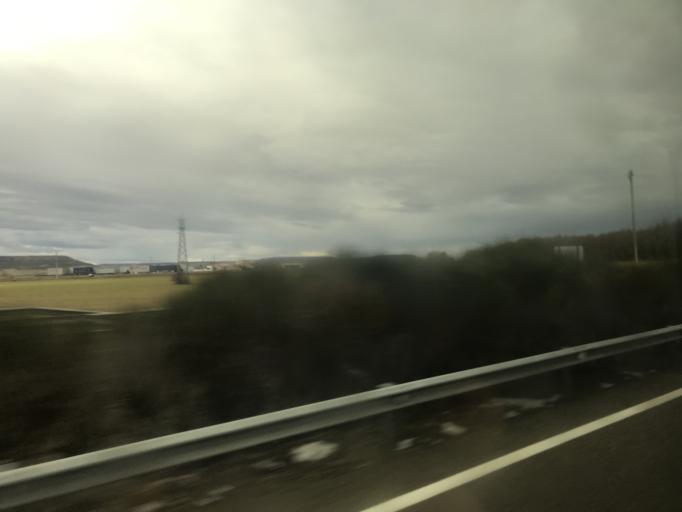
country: ES
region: Castille and Leon
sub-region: Provincia de Palencia
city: Torquemada
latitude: 42.0290
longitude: -4.3143
